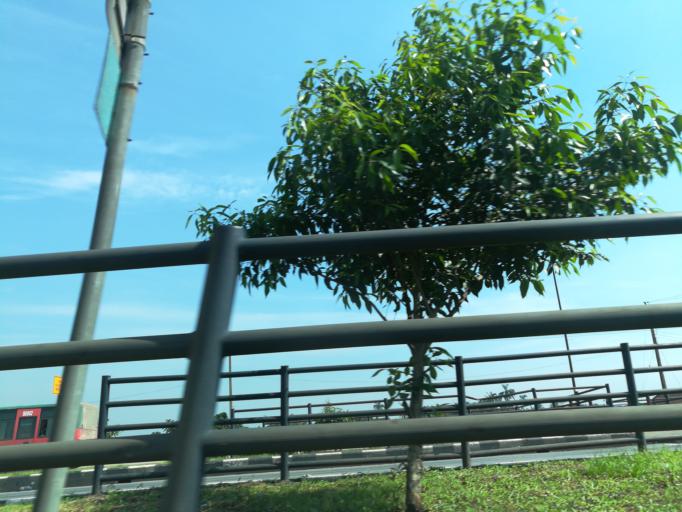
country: NG
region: Lagos
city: Ojota
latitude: 6.6089
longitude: 3.4260
